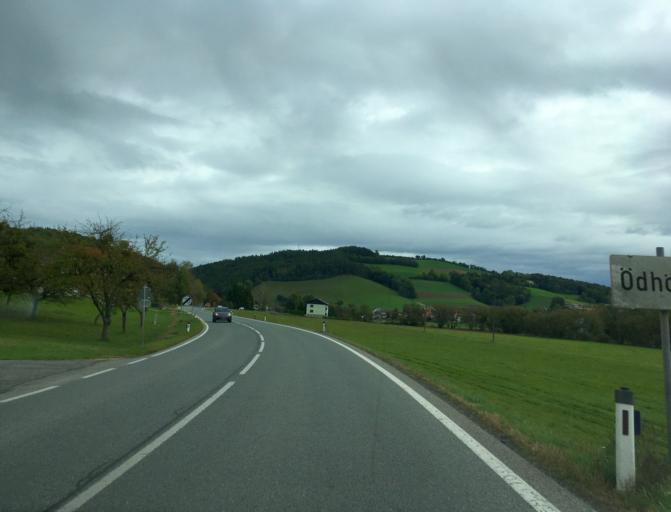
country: AT
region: Lower Austria
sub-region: Politischer Bezirk Wiener Neustadt
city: Bad Schonau
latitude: 47.4959
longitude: 16.2226
